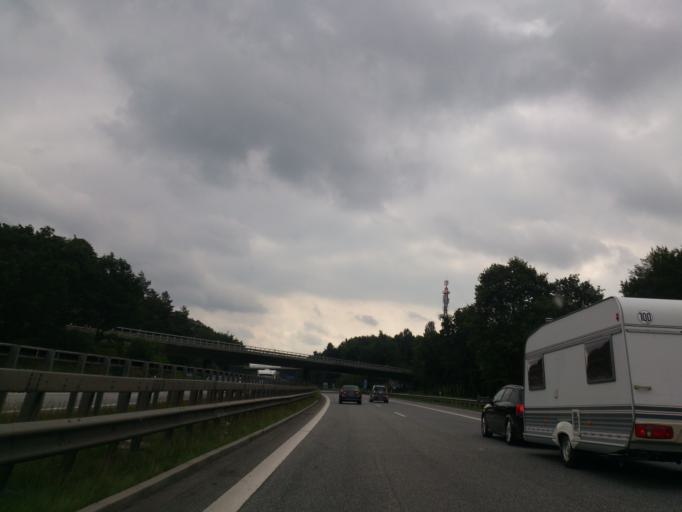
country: DE
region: Lower Saxony
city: Seevetal
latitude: 53.4368
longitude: 9.9250
